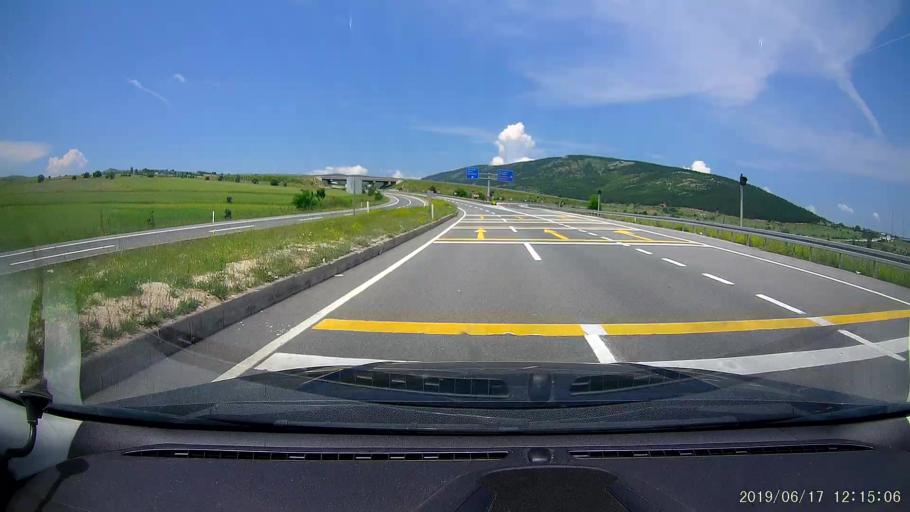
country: TR
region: Karabuk
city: Gozyeri
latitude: 40.8710
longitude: 32.5838
